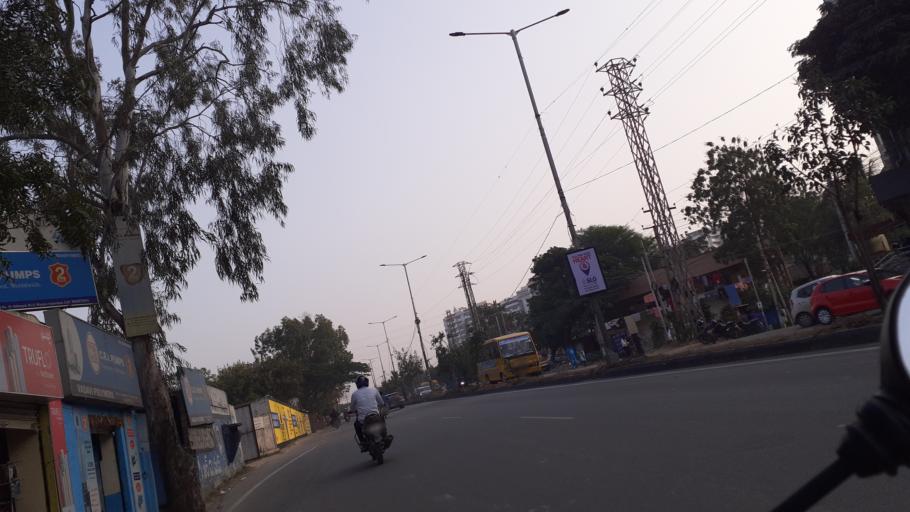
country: IN
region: Telangana
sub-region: Medak
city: Serilingampalle
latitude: 17.4913
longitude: 78.3535
